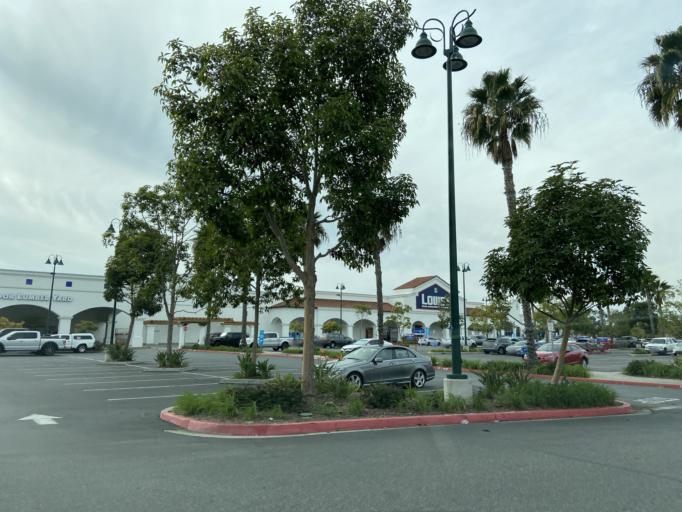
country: US
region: California
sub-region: San Diego County
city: Camp Pendleton South
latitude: 33.2307
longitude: -117.3078
